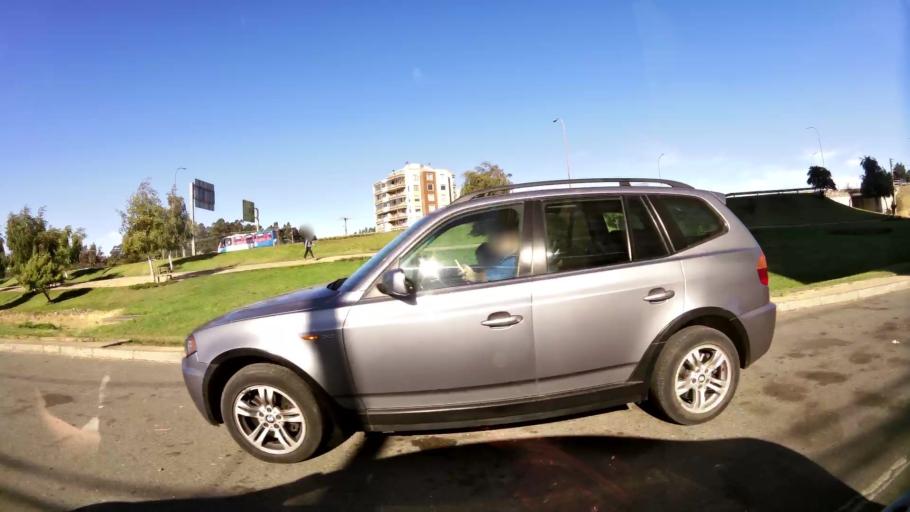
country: CL
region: Biobio
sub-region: Provincia de Concepcion
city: Concepcion
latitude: -36.8366
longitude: -73.1017
